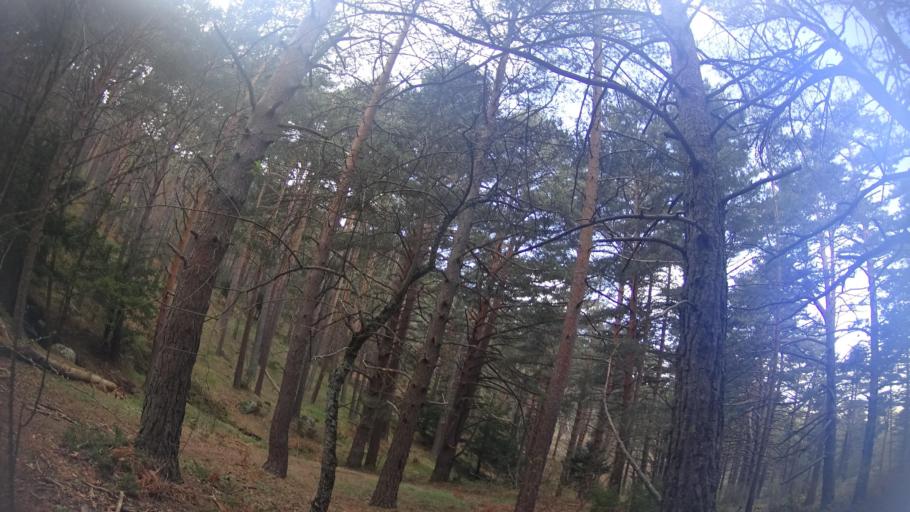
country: ES
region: Madrid
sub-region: Provincia de Madrid
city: Canencia
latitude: 40.8735
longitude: -3.7671
